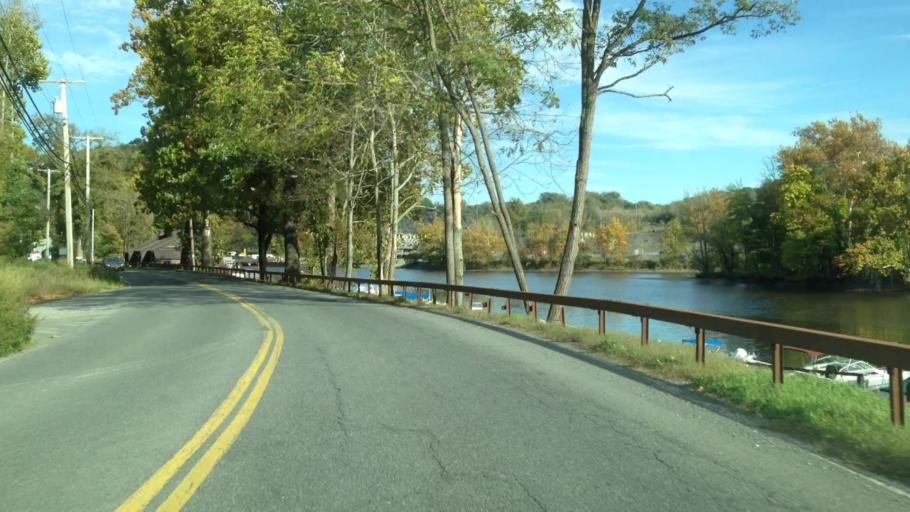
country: US
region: New York
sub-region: Ulster County
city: Kingston
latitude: 41.9040
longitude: -74.0102
